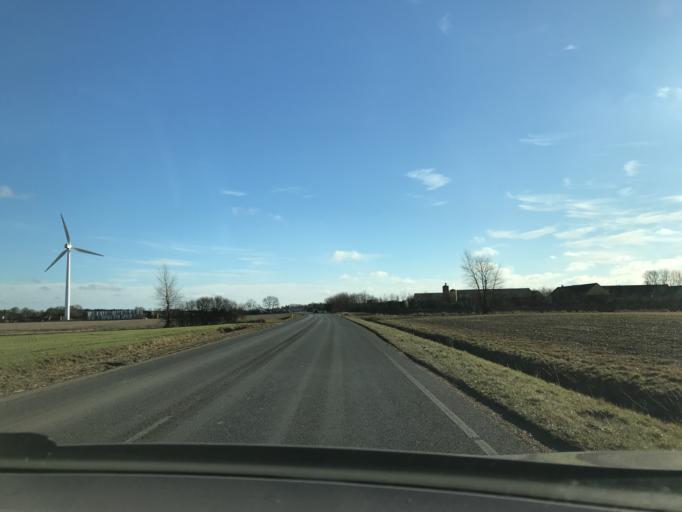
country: DK
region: South Denmark
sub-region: Middelfart Kommune
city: Strib
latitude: 55.5020
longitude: 9.8027
